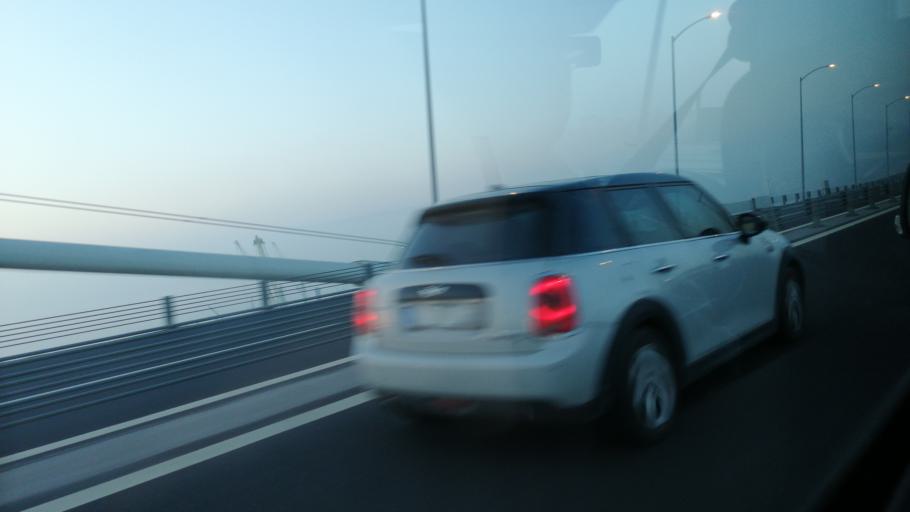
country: TR
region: Kocaeli
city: Tavsanli
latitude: 40.7663
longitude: 29.5177
